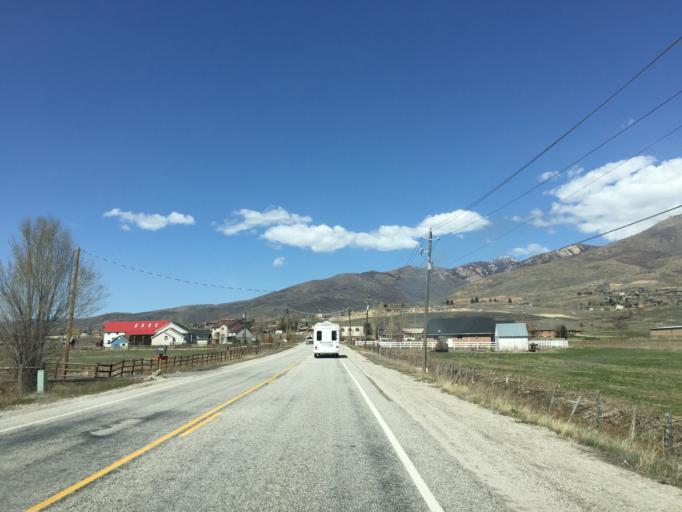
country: US
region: Utah
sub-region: Weber County
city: Wolf Creek
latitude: 41.3113
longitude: -111.8252
